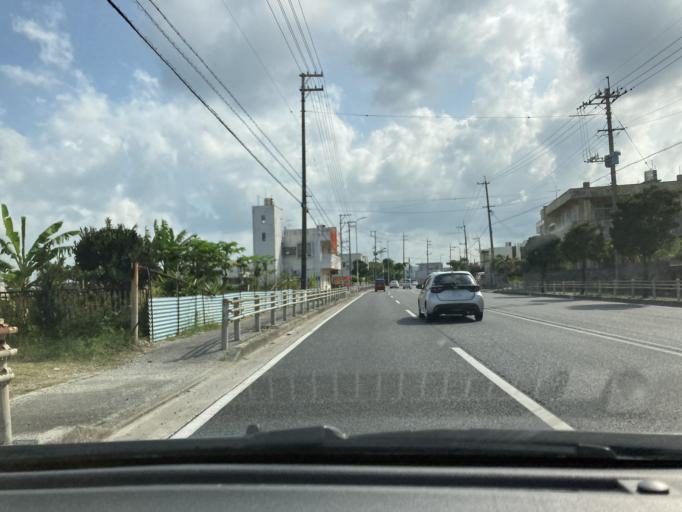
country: JP
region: Okinawa
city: Ginowan
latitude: 26.2462
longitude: 127.7817
